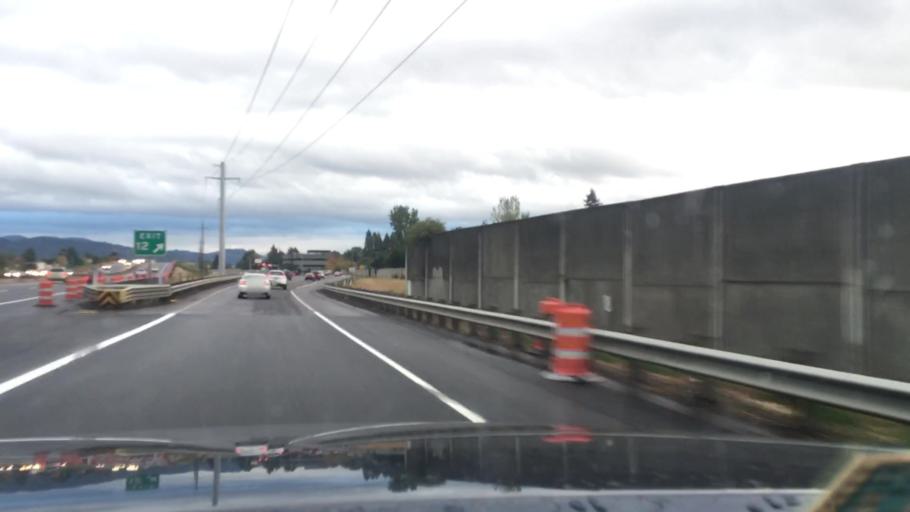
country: US
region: Oregon
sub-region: Lane County
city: Eugene
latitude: 44.0877
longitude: -123.0745
